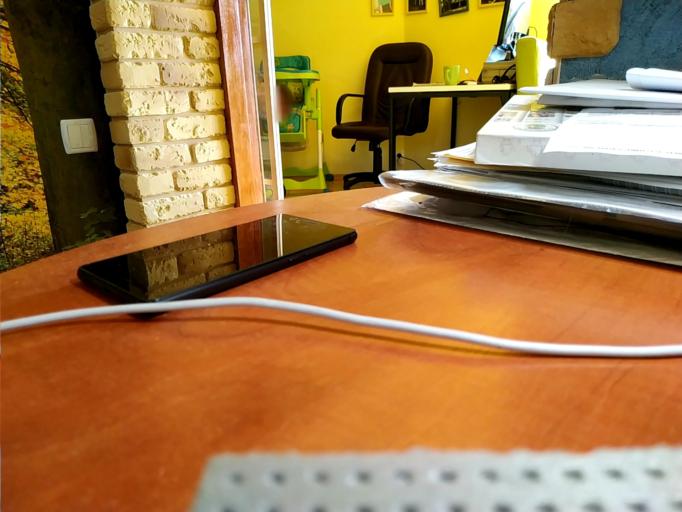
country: RU
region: Tverskaya
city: Kalashnikovo
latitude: 57.3661
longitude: 35.4413
